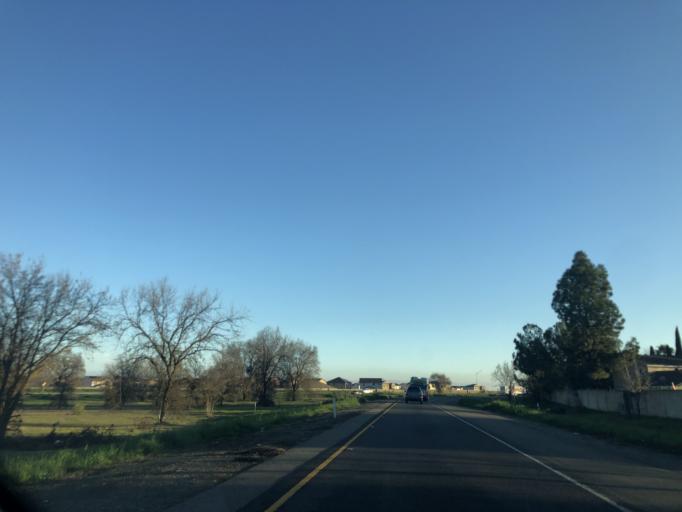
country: US
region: California
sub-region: Yolo County
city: Woodland
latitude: 38.6618
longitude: -121.7535
